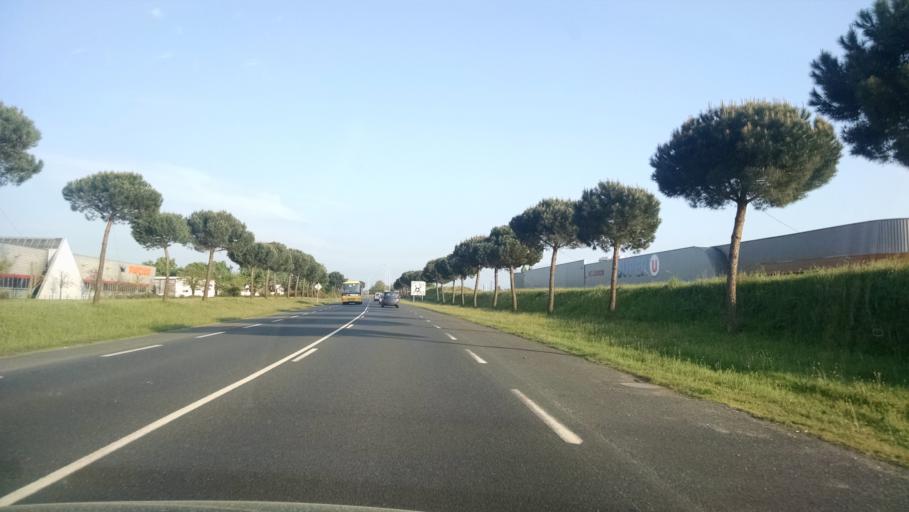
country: FR
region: Pays de la Loire
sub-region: Departement de la Loire-Atlantique
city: Getigne
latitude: 47.0863
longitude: -1.2611
